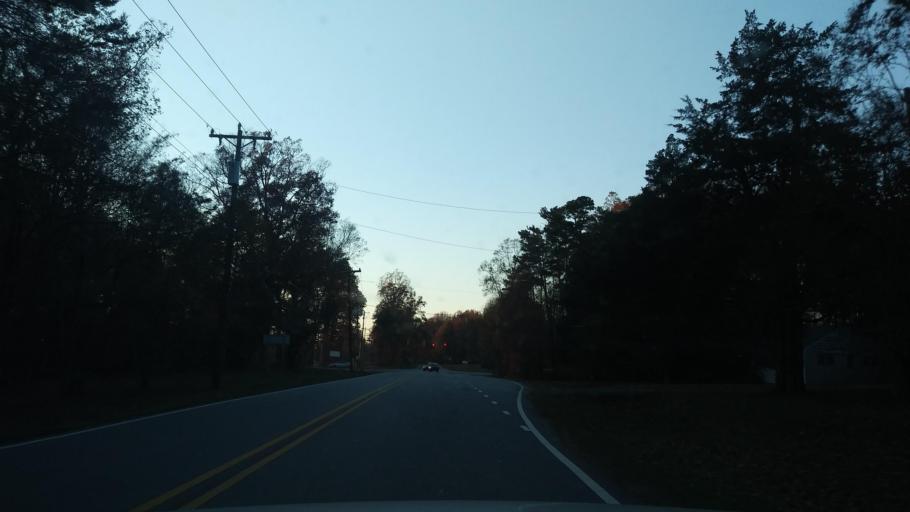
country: US
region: North Carolina
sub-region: Guilford County
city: Pleasant Garden
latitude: 35.9920
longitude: -79.7917
